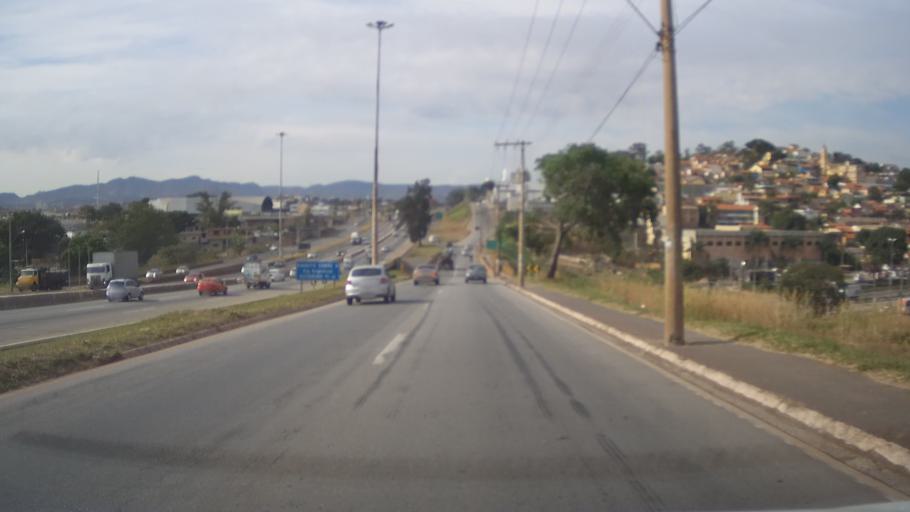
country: BR
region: Minas Gerais
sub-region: Contagem
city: Contagem
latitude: -19.9314
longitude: -44.0076
